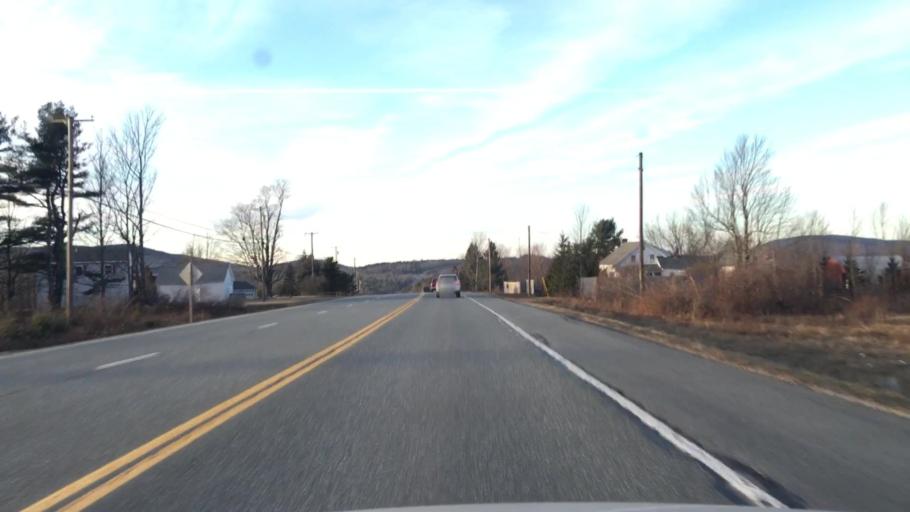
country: US
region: Maine
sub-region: Hancock County
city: Surry
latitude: 44.6252
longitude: -68.5342
